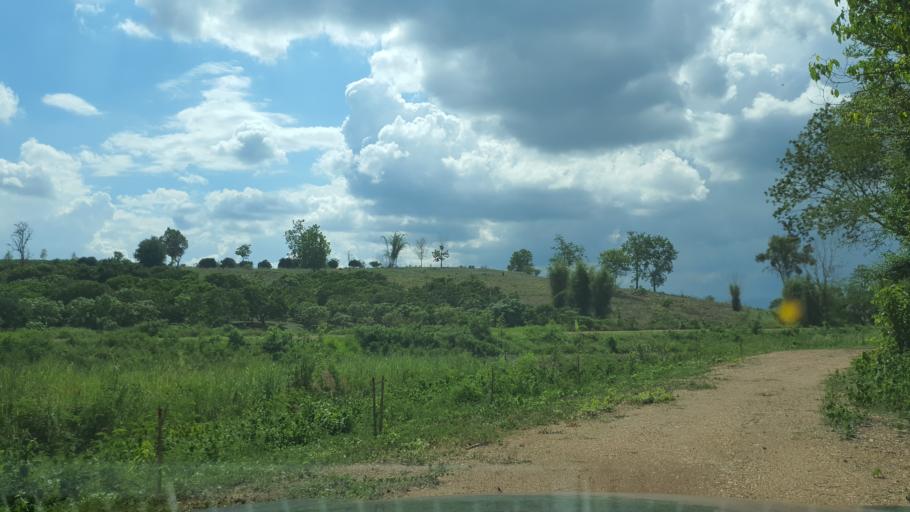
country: TH
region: Chiang Mai
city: Mae Taeng
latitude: 19.0899
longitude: 99.0795
